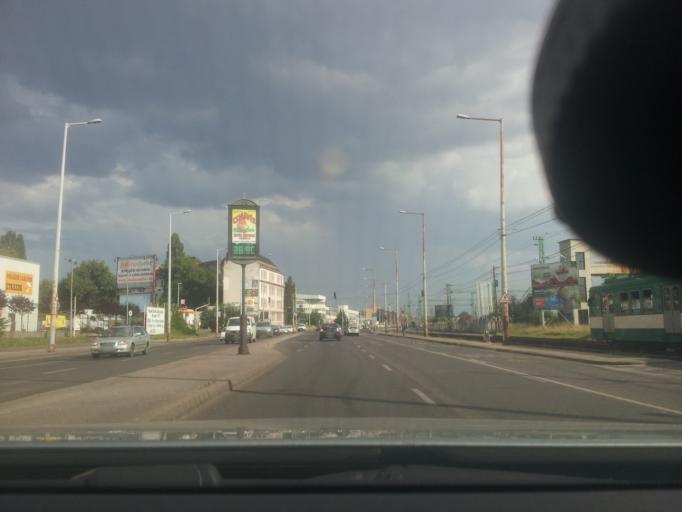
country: HU
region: Budapest
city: Budapest XX. keruelet
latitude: 47.4566
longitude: 19.0854
